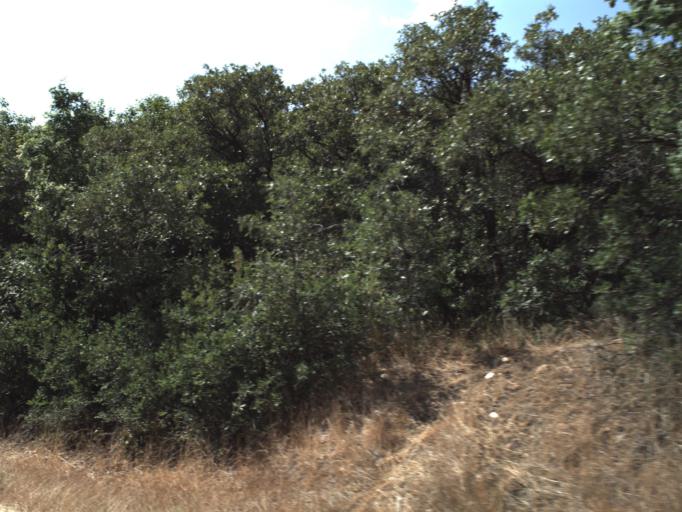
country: US
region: Utah
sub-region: Weber County
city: Wolf Creek
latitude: 41.2647
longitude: -111.6896
